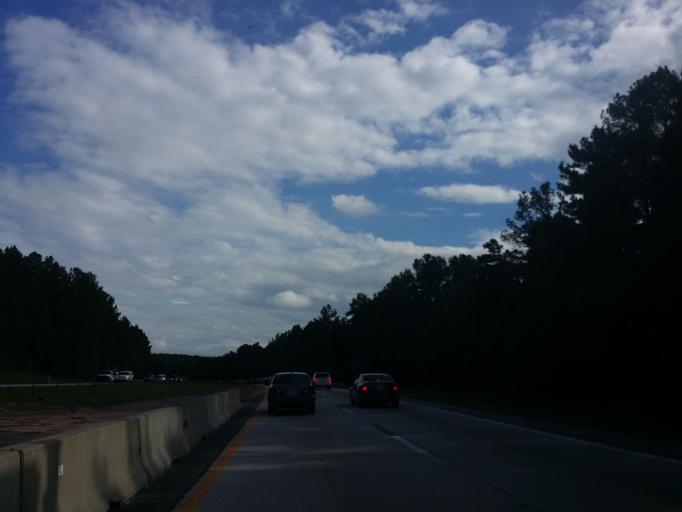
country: US
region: North Carolina
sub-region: Durham County
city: Durham
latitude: 35.9513
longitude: -78.8643
